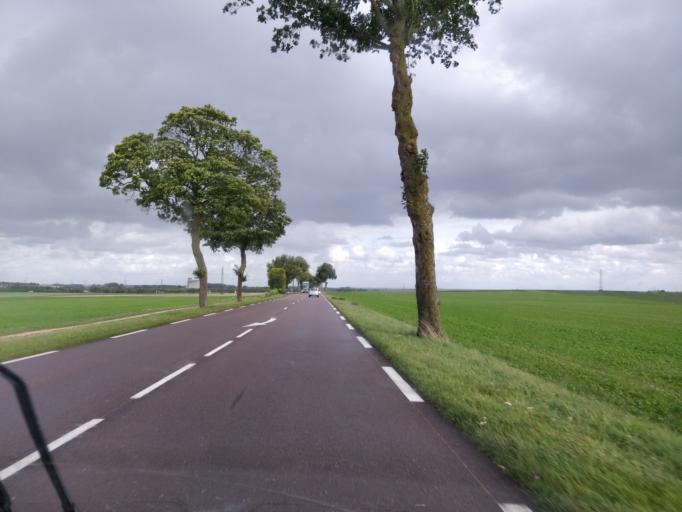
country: FR
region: Champagne-Ardenne
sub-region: Departement de l'Aube
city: Saint-Parres-aux-Tertres
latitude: 48.2933
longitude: 4.1453
